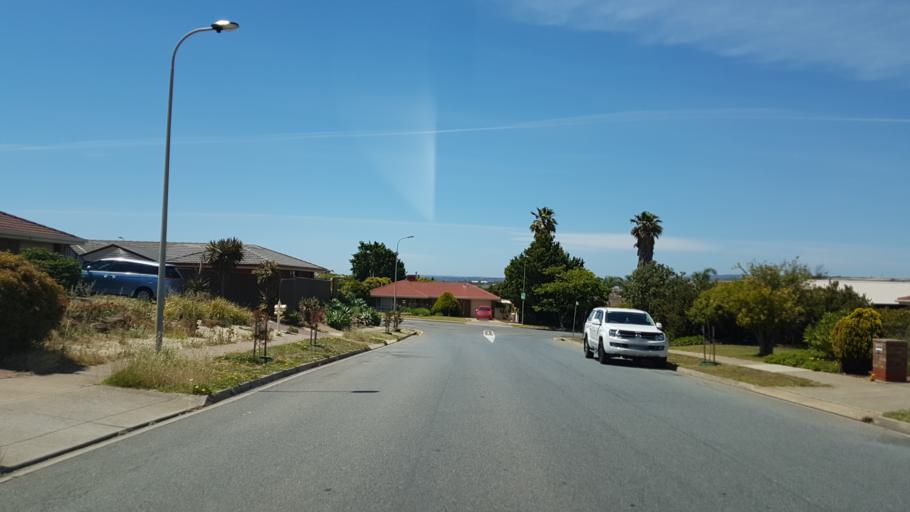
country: AU
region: South Australia
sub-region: Onkaparinga
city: Moana
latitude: -35.2141
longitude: 138.4753
